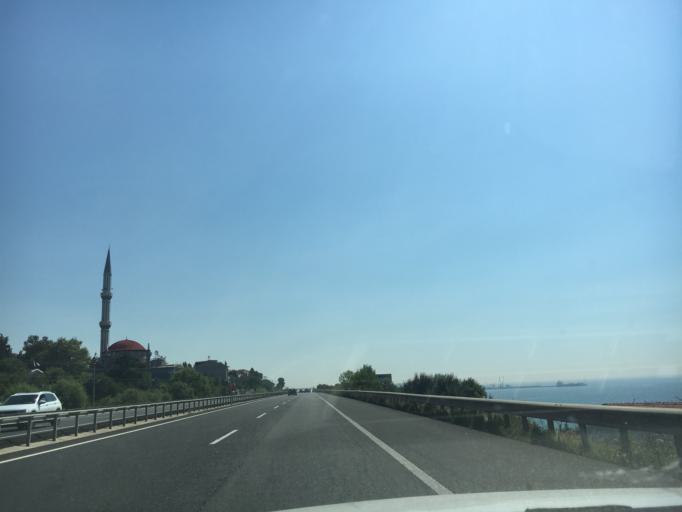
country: TR
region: Tekirdag
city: Marmara Ereglisi
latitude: 40.9692
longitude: 27.9003
